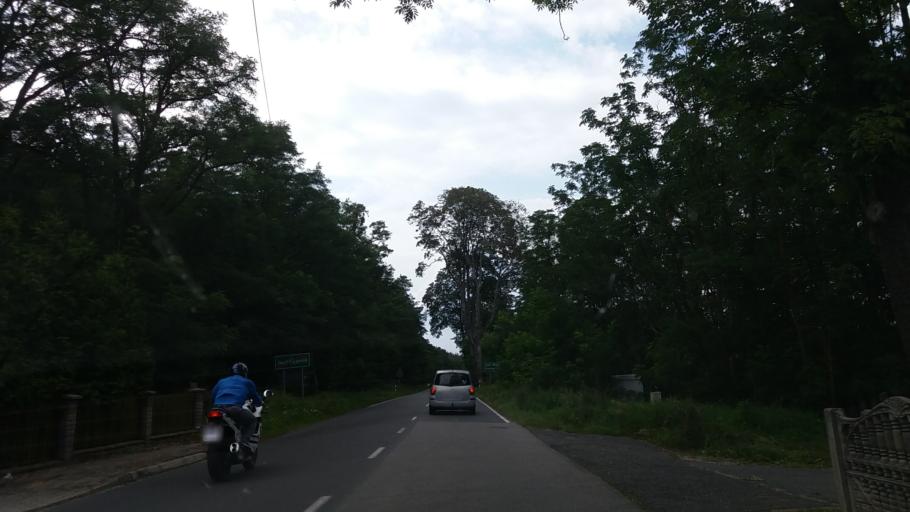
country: PL
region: Lubusz
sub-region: Powiat strzelecko-drezdenecki
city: Zwierzyn
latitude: 52.7243
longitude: 15.5857
